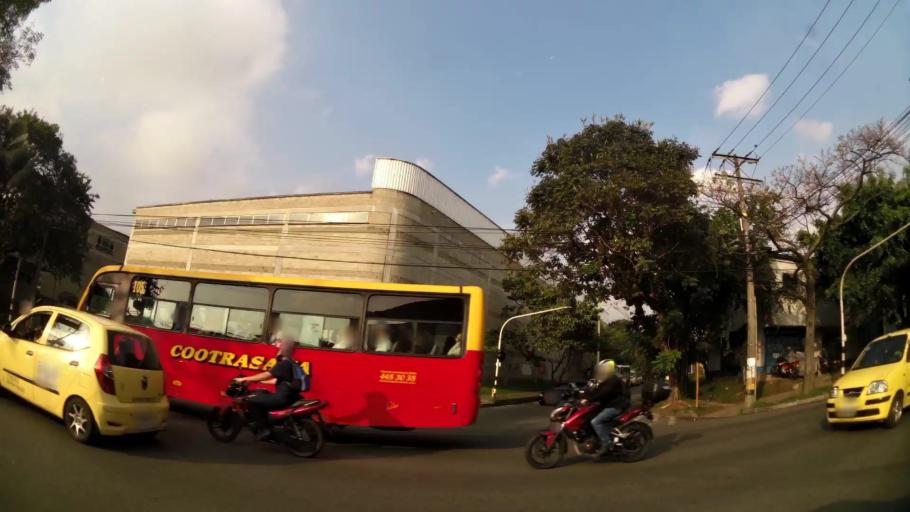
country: CO
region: Antioquia
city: Sabaneta
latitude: 6.1639
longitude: -75.6156
